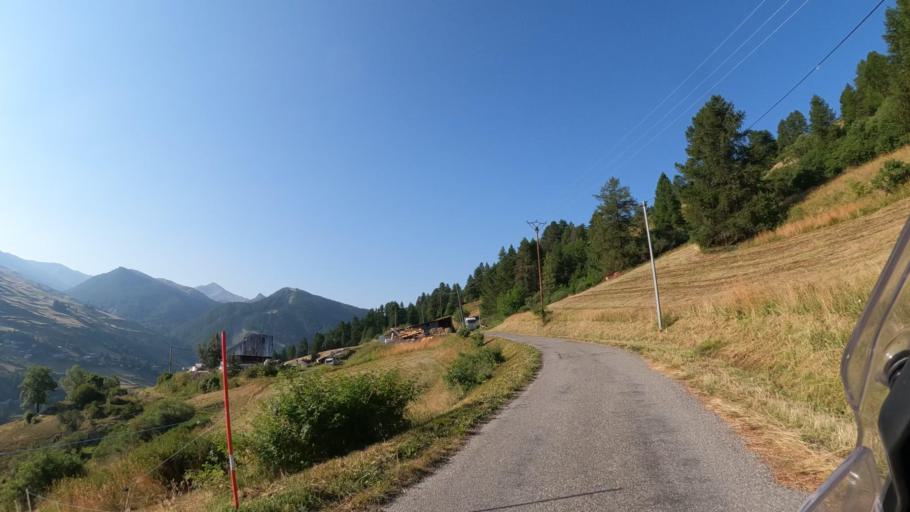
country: FR
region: Provence-Alpes-Cote d'Azur
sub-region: Departement des Hautes-Alpes
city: Guillestre
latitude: 44.6042
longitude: 6.6815
